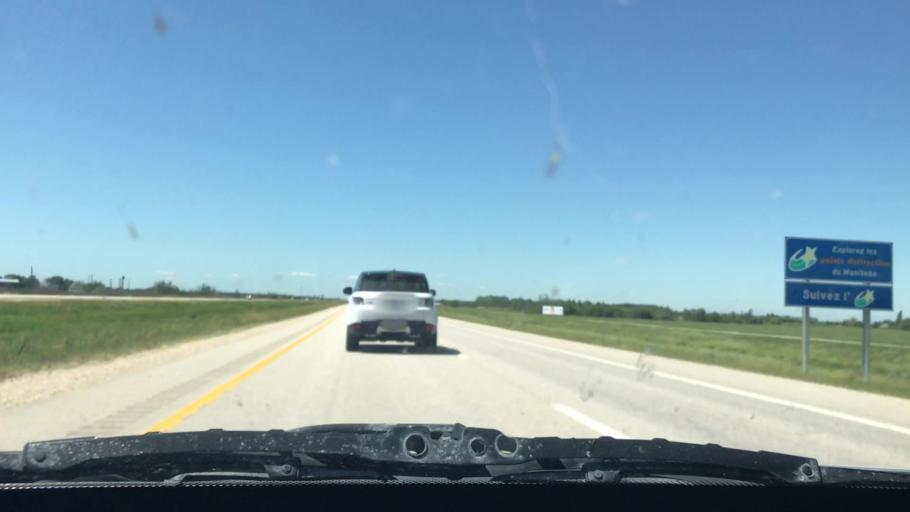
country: CA
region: Manitoba
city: Niverville
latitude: 49.8045
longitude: -96.8975
